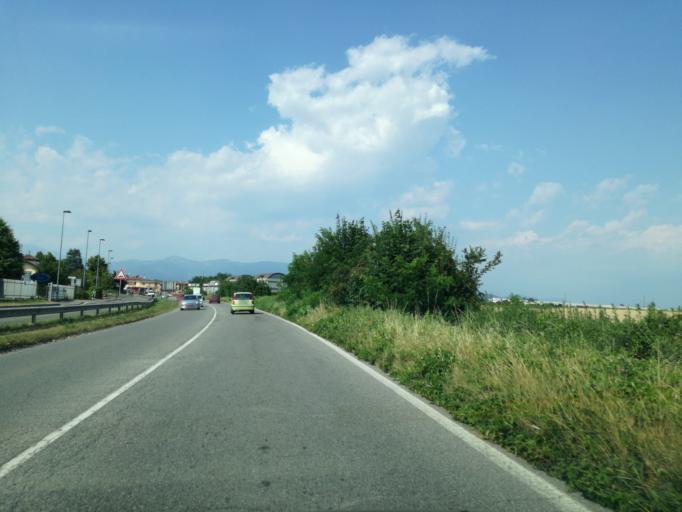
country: IT
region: Lombardy
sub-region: Provincia di Lecco
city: Osnago
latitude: 45.6744
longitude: 9.3945
